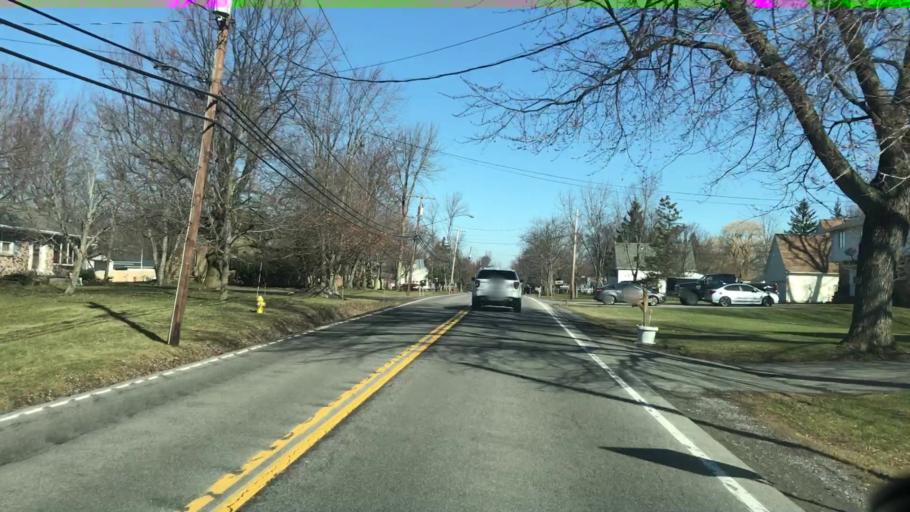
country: US
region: New York
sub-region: Erie County
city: Lancaster
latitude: 42.8710
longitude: -78.6764
